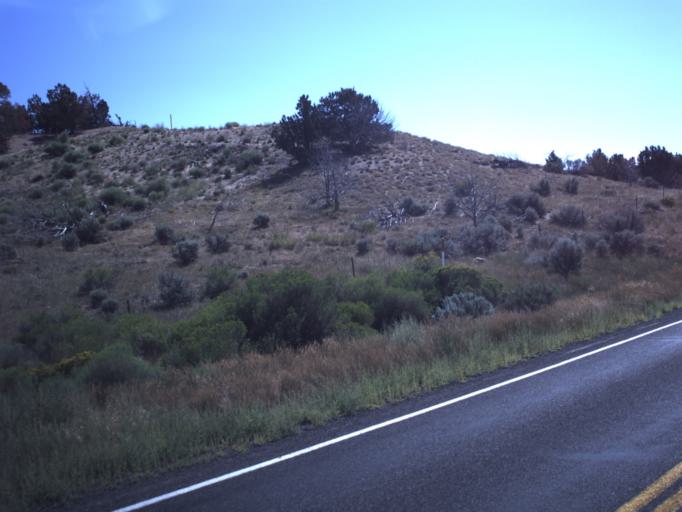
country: US
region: Utah
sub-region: Utah County
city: Genola
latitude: 39.9545
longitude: -112.2404
